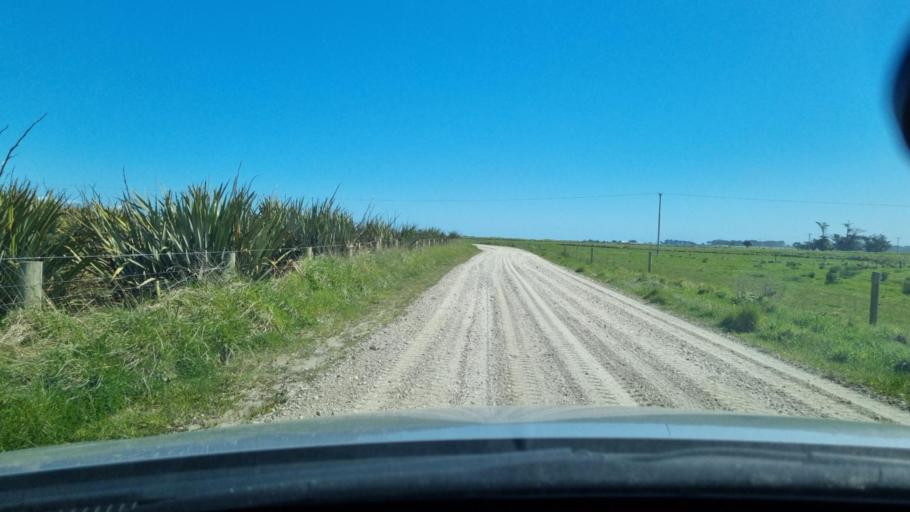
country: NZ
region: Southland
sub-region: Invercargill City
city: Invercargill
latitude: -46.3916
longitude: 168.2598
